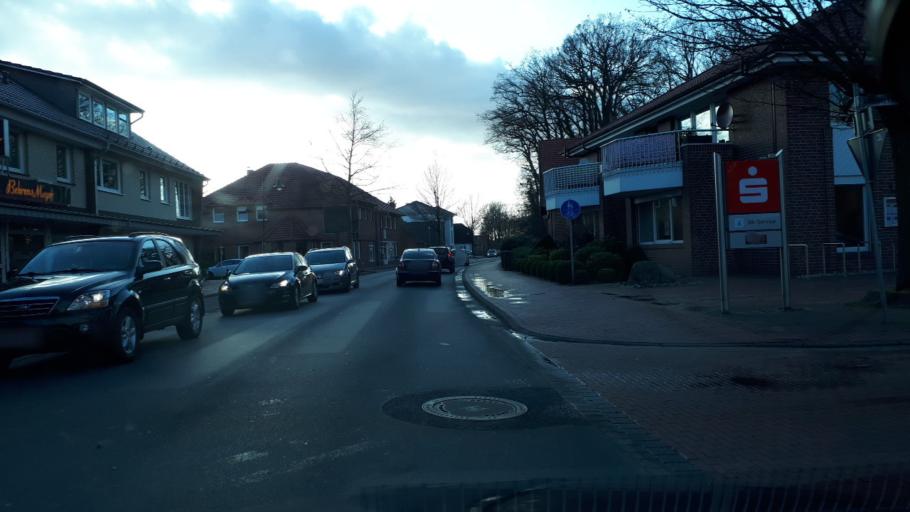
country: DE
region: Lower Saxony
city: Molbergen
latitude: 52.8587
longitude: 7.9214
